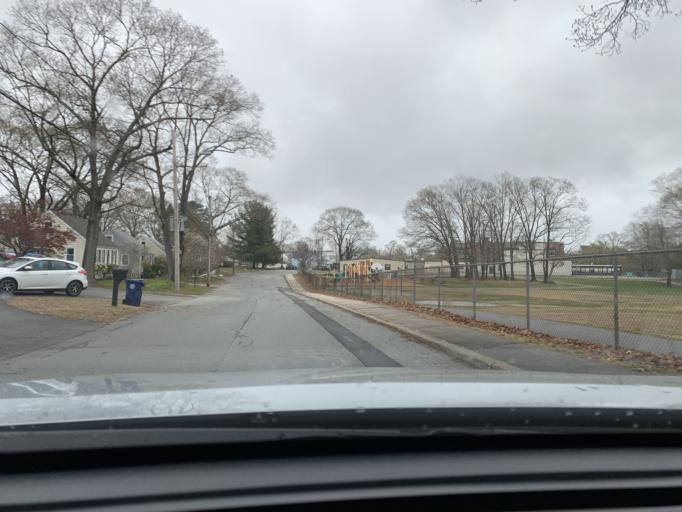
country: US
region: Rhode Island
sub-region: Kent County
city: Warwick
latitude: 41.6985
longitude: -71.4017
